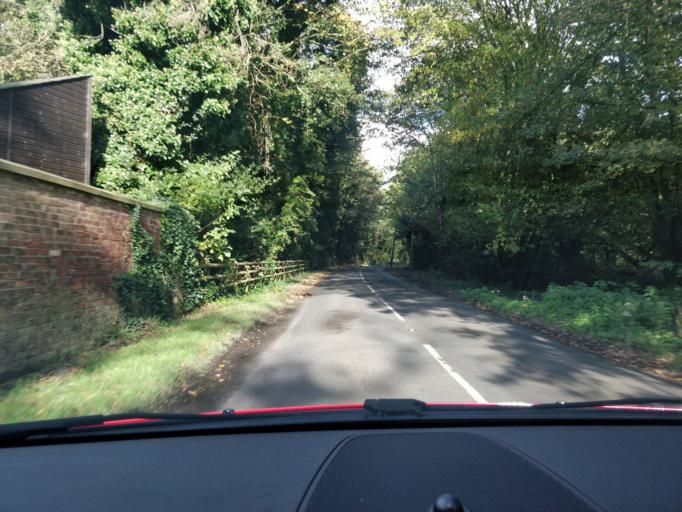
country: GB
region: England
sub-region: Lancashire
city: Ormskirk
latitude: 53.5826
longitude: -2.8492
